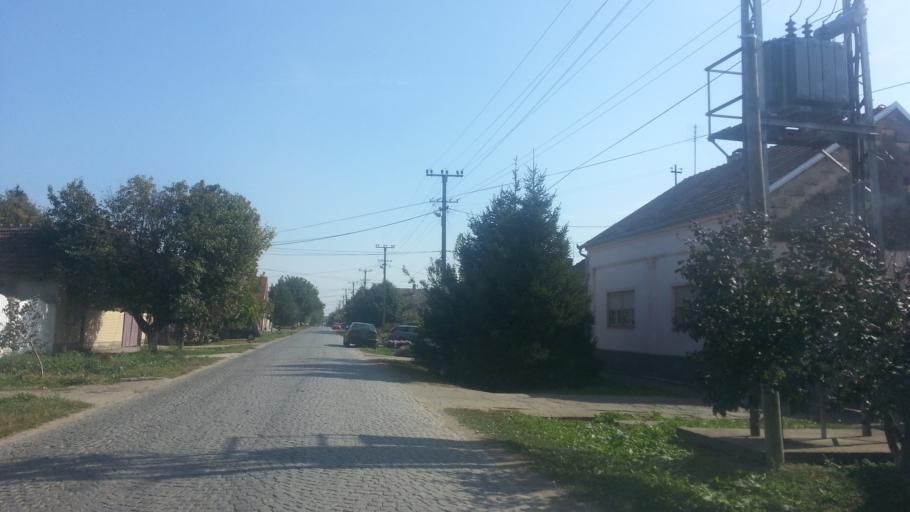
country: RS
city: Stari Banovci
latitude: 44.9961
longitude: 20.2816
